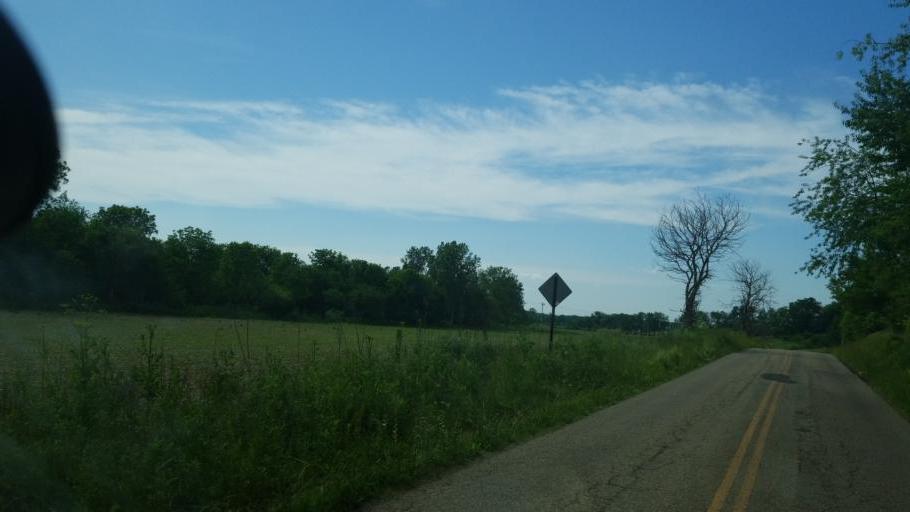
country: US
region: Ohio
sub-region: Knox County
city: Gambier
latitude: 40.2952
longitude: -82.3565
